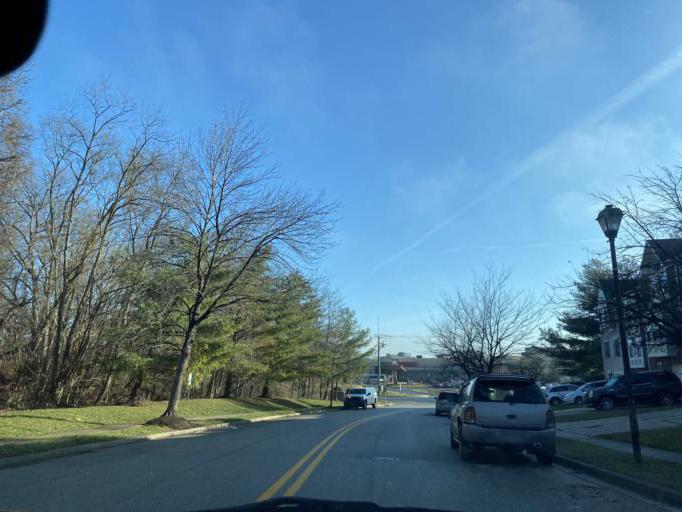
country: US
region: Maryland
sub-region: Prince George's County
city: West Laurel
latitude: 39.0872
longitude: -76.8857
